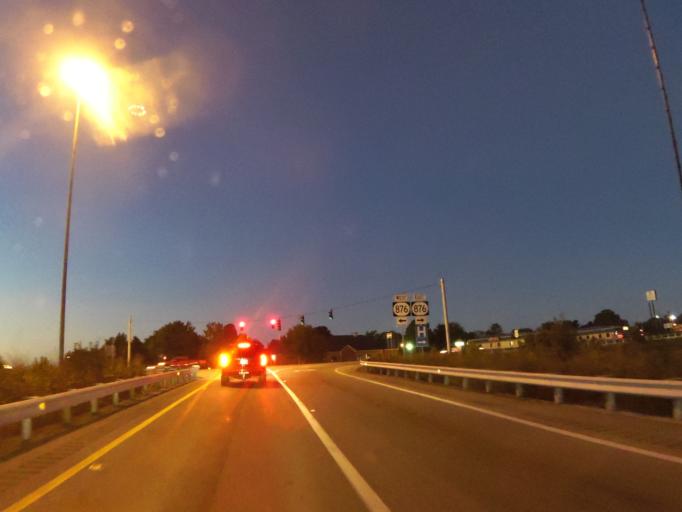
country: US
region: Kentucky
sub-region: Madison County
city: Richmond
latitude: 37.7357
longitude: -84.3226
